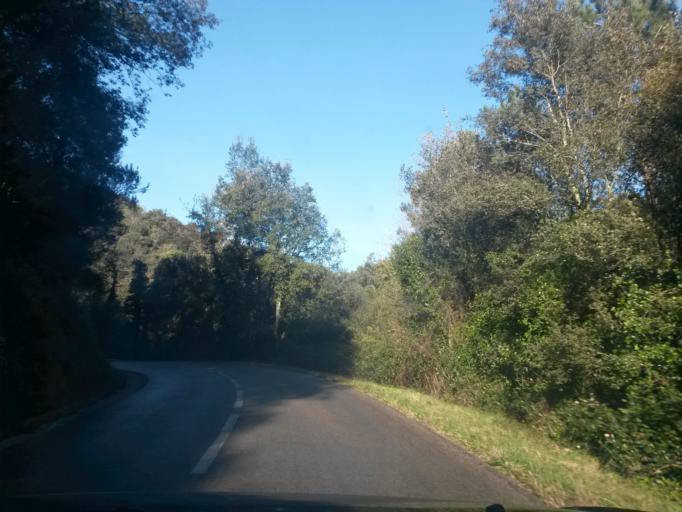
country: ES
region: Catalonia
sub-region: Provincia de Girona
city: Sant Gregori
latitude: 41.9858
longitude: 2.6863
